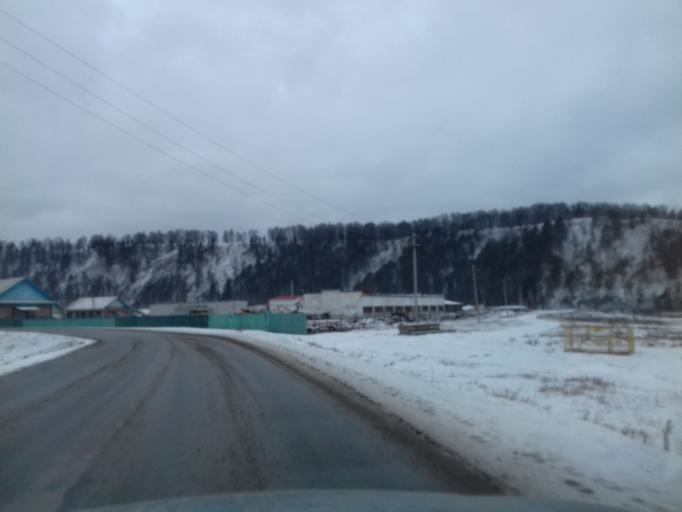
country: RU
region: Bashkortostan
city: Starosubkhangulovo
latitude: 53.0940
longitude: 57.4279
